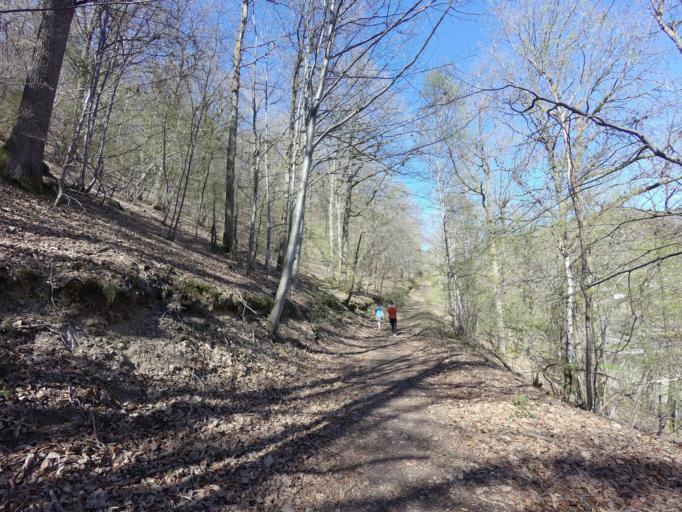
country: BE
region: Wallonia
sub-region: Province de Liege
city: Trois-Ponts
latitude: 50.3894
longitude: 5.8706
